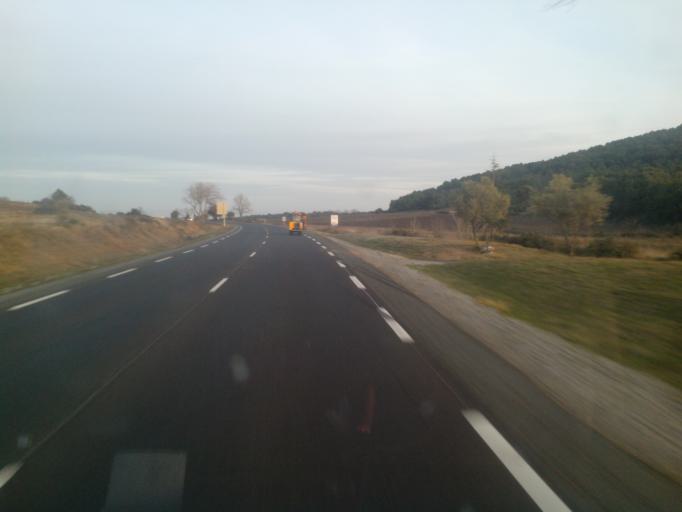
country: FR
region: Languedoc-Roussillon
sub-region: Departement de l'Herault
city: Olonzac
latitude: 43.2746
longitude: 2.7778
